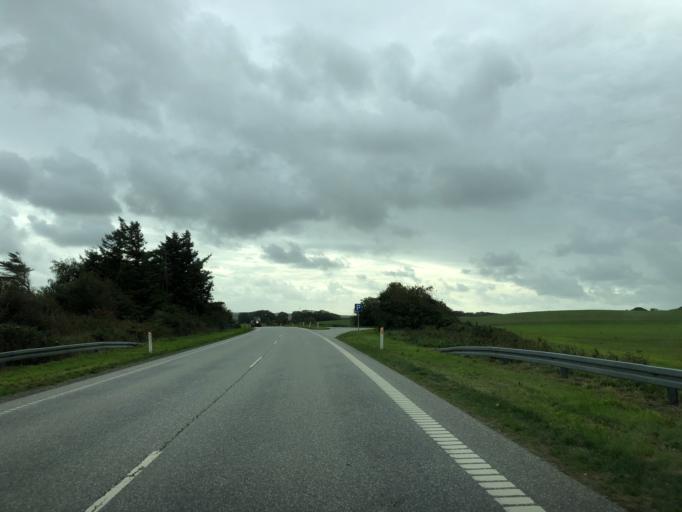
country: DK
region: North Denmark
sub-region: Thisted Kommune
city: Hurup
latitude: 56.8012
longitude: 8.4738
